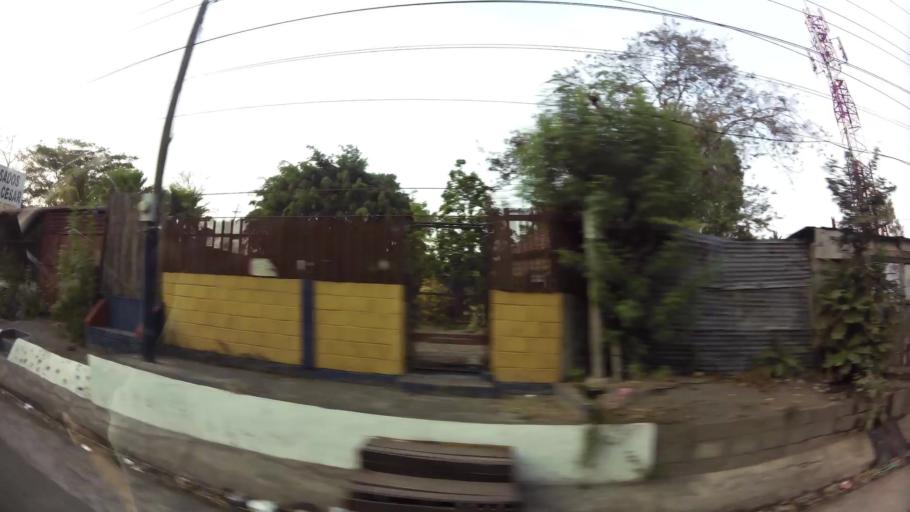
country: NI
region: Managua
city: Ciudad Sandino
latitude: 12.1385
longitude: -86.3303
